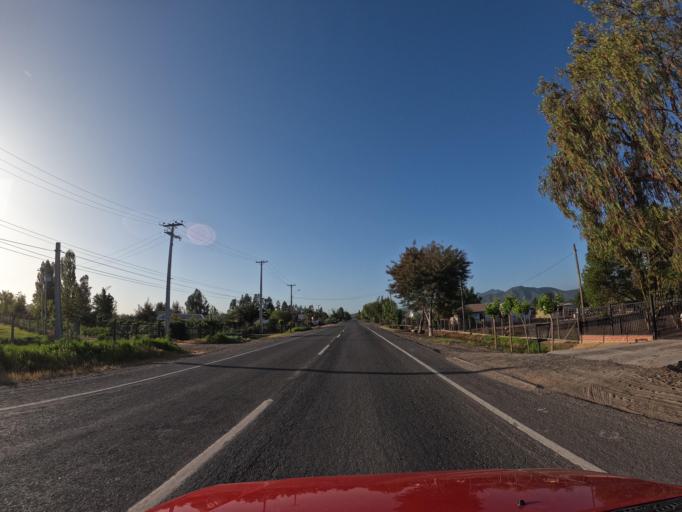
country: CL
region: O'Higgins
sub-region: Provincia de Colchagua
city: Santa Cruz
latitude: -34.4542
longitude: -71.3650
